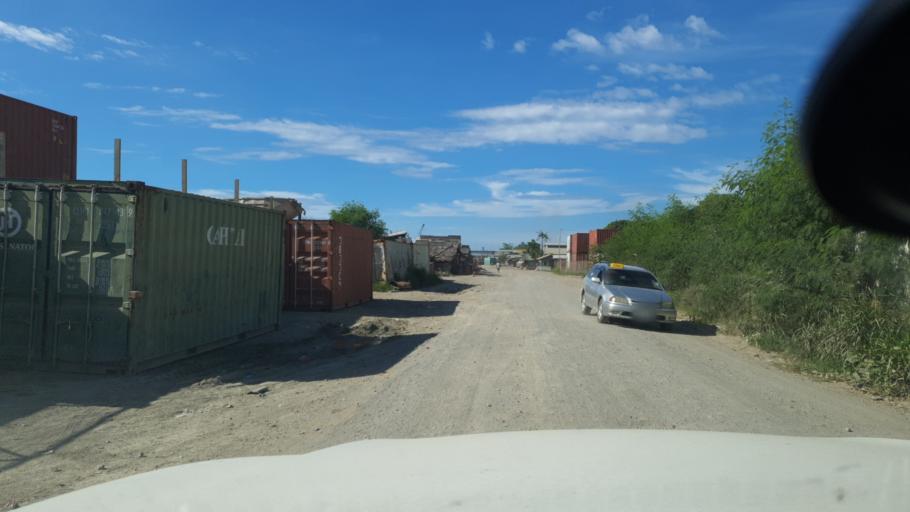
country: SB
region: Guadalcanal
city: Honiara
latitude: -9.4246
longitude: 160.0063
